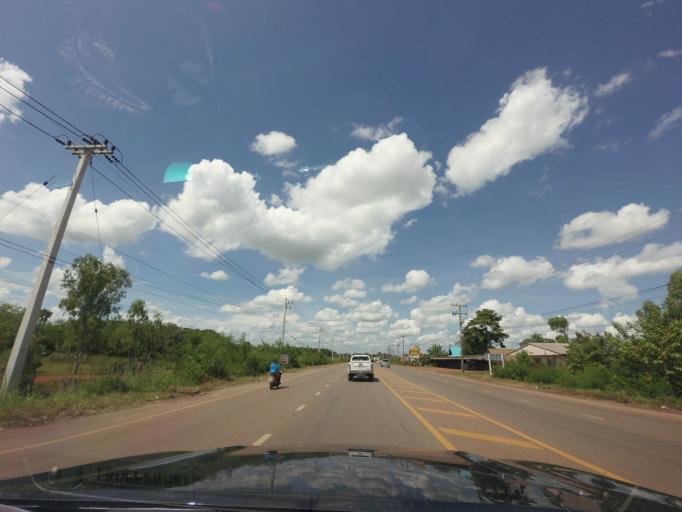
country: TH
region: Changwat Udon Thani
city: Ban Dung
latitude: 17.7200
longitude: 103.2501
